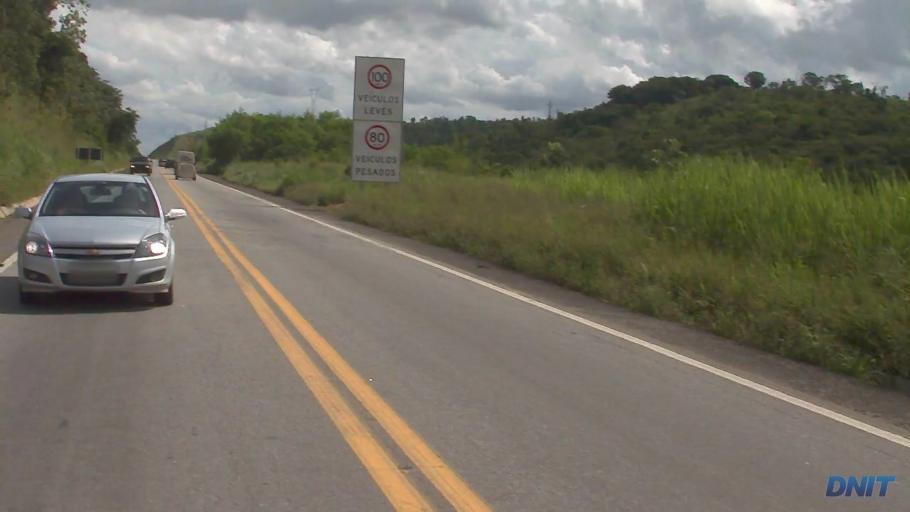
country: BR
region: Minas Gerais
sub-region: Ipaba
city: Ipaba
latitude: -19.4086
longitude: -42.4874
